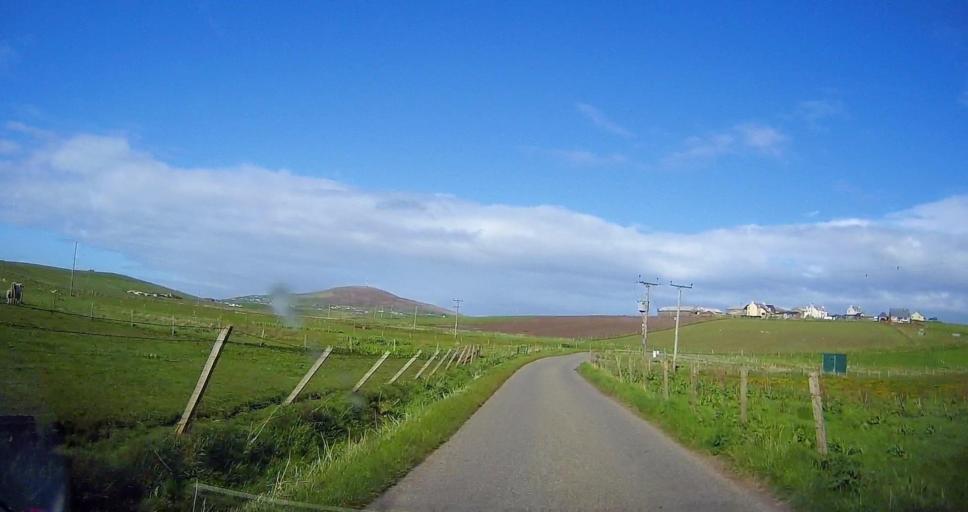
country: GB
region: Scotland
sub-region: Shetland Islands
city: Sandwick
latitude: 59.9106
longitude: -1.3319
